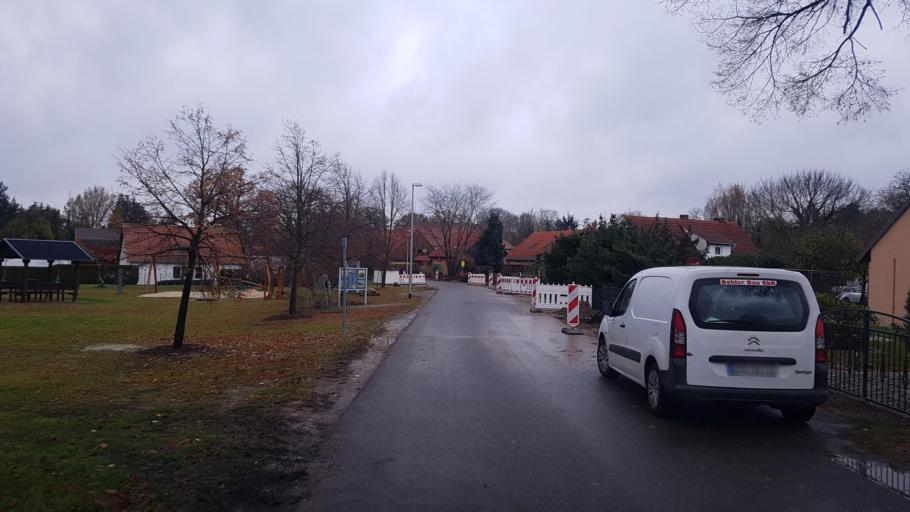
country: DE
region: Brandenburg
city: Drebkau
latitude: 51.6959
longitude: 14.1963
